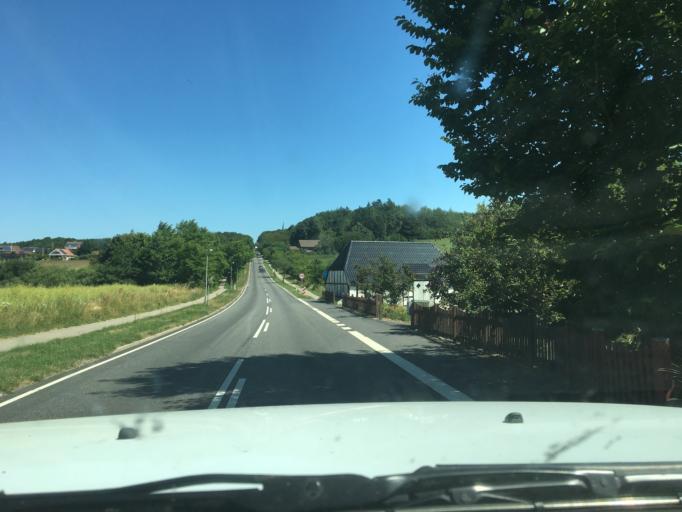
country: DK
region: Central Jutland
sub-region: Horsens Kommune
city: Braedstrup
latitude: 55.9613
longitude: 9.6019
